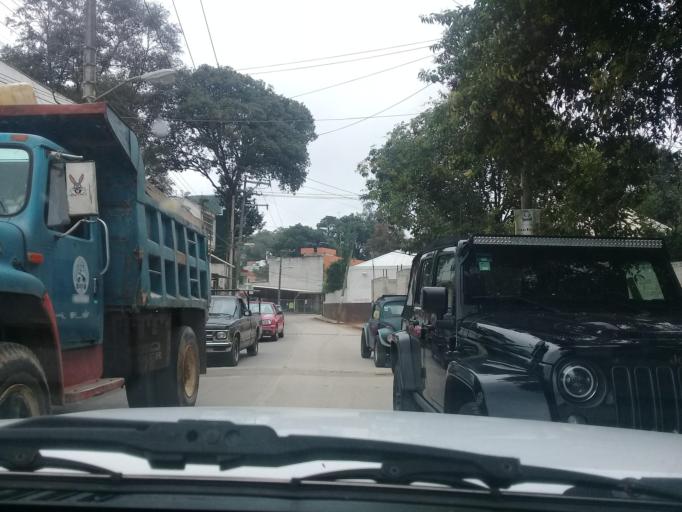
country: MX
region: Veracruz
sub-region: Xalapa
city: Lomas Verdes
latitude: 19.5093
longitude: -96.9066
